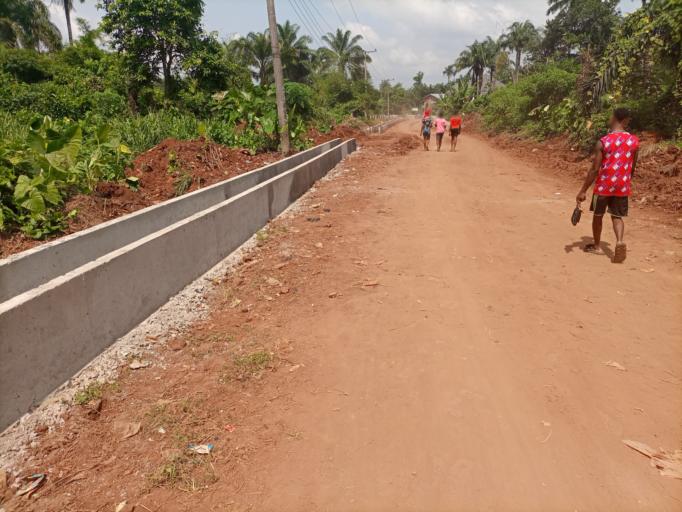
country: NG
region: Imo
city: Ihuo
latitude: 5.5262
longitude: 7.2626
